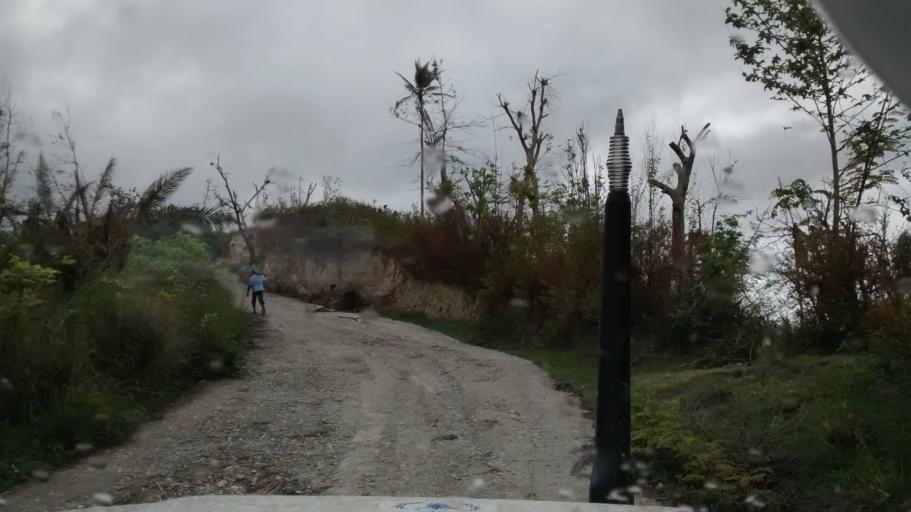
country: HT
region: Grandans
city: Jeremie
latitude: 18.5889
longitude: -74.1435
